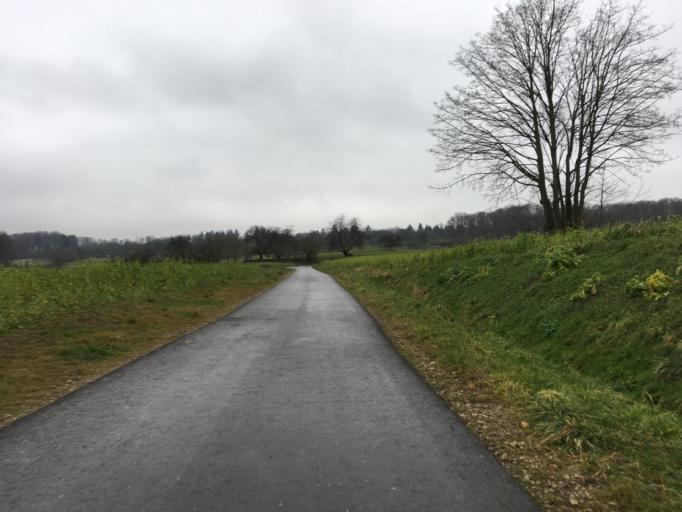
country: DE
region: Baden-Wuerttemberg
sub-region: Karlsruhe Region
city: Konigsbach-Stein
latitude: 48.9467
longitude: 8.5289
